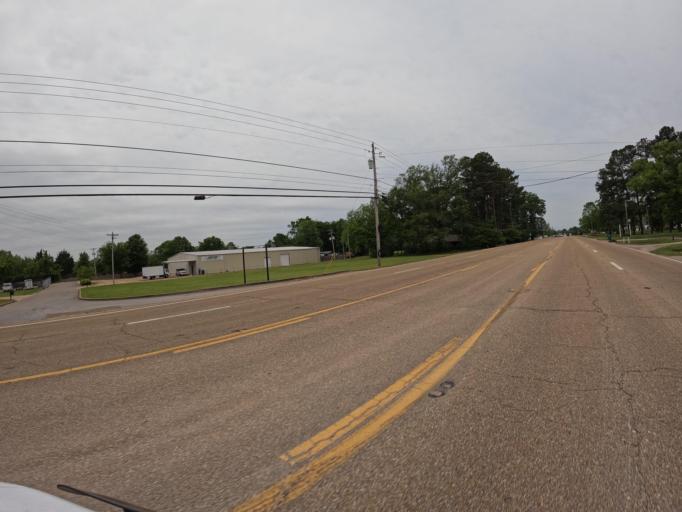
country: US
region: Mississippi
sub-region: Lee County
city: Tupelo
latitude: 34.2938
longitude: -88.7600
